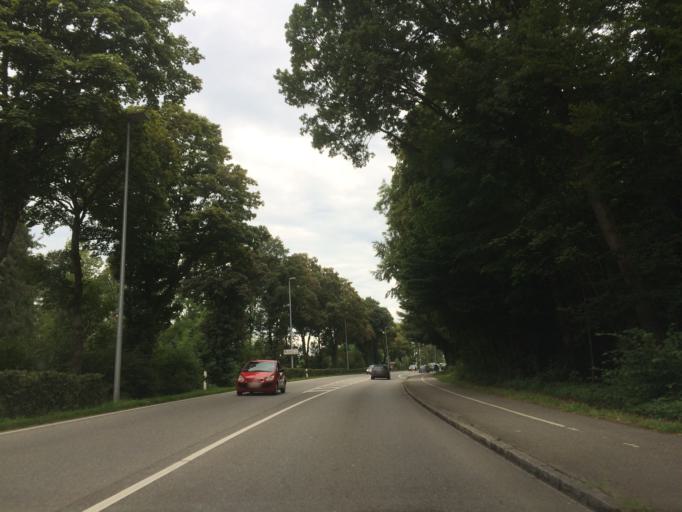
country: DE
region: Baden-Wuerttemberg
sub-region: Tuebingen Region
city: Friedrichshafen
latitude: 47.6599
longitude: 9.4360
